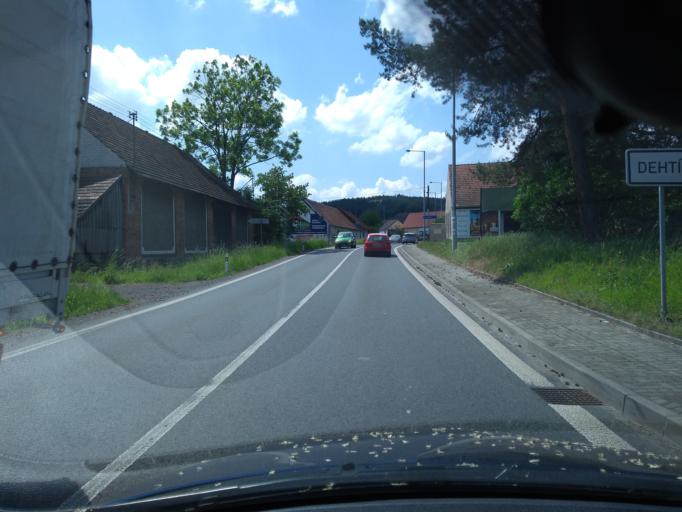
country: CZ
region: Plzensky
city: Svihov
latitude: 49.4487
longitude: 13.2883
